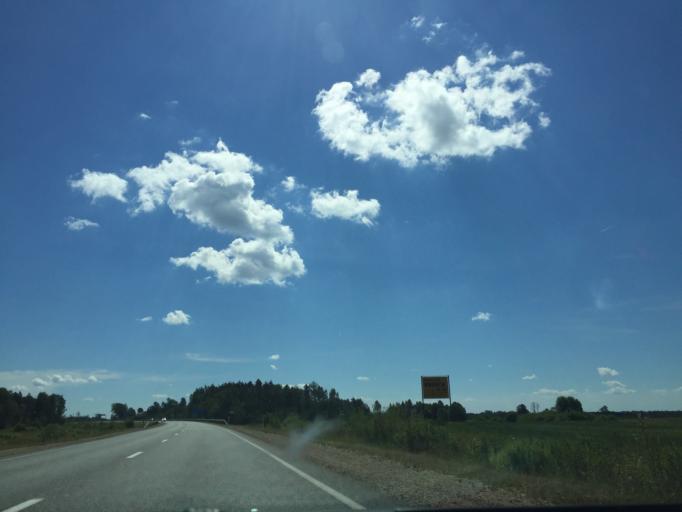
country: LV
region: Koknese
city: Koknese
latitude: 56.6694
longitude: 25.4050
